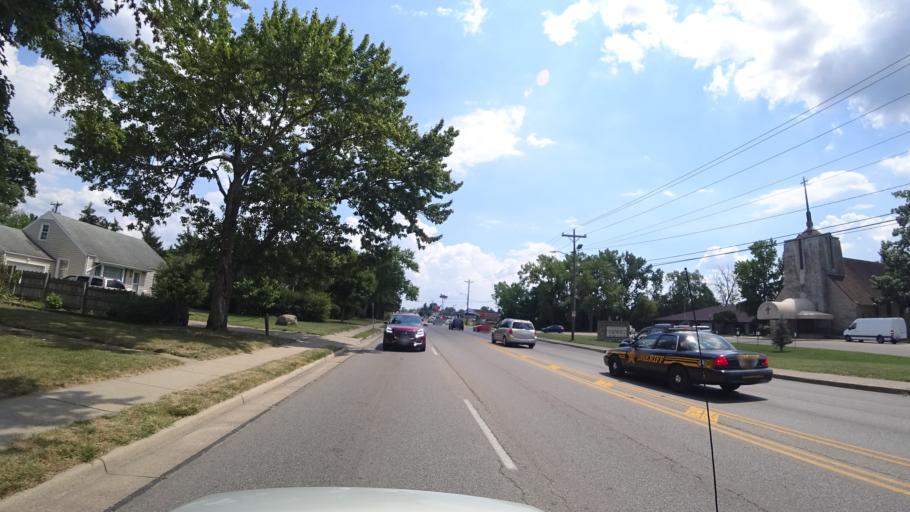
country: US
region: Ohio
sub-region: Butler County
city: Hamilton
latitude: 39.4192
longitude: -84.5884
